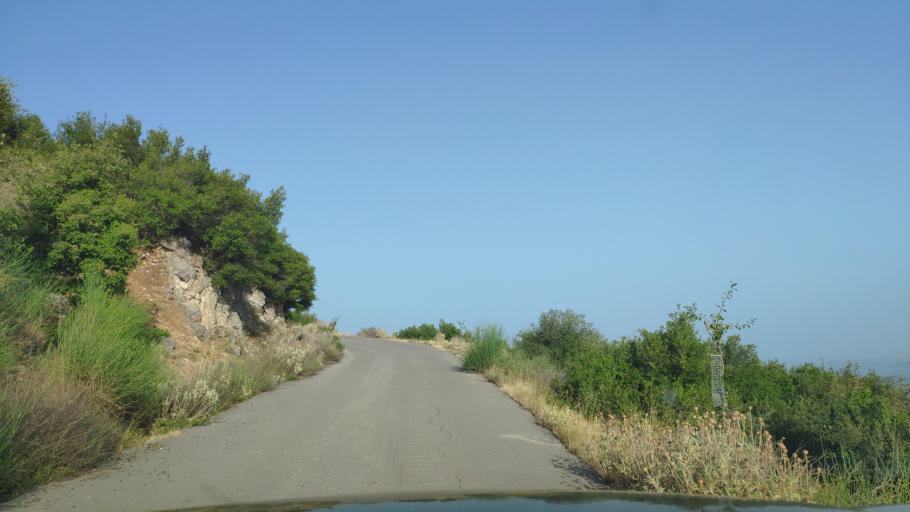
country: GR
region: West Greece
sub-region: Nomos Aitolias kai Akarnanias
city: Monastirakion
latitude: 38.8479
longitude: 20.9734
